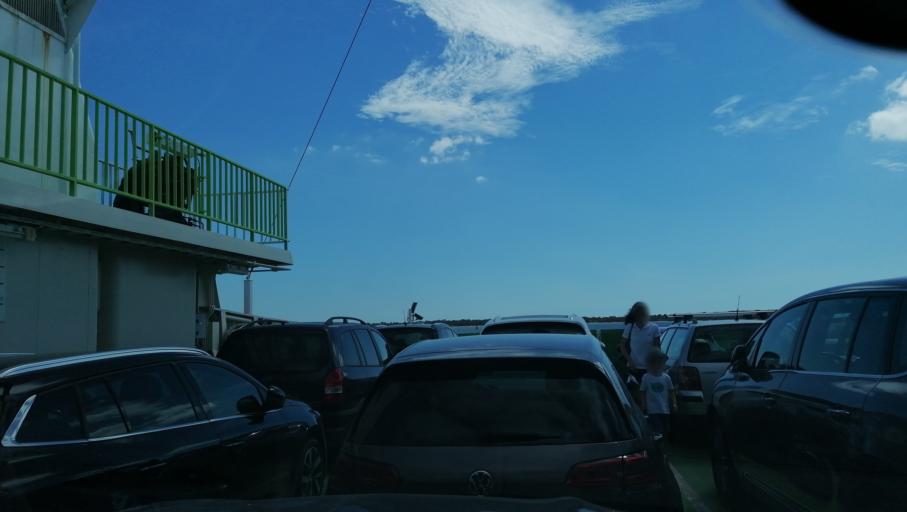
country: PT
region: Setubal
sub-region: Setubal
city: Setubal
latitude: 38.5038
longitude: -8.8856
